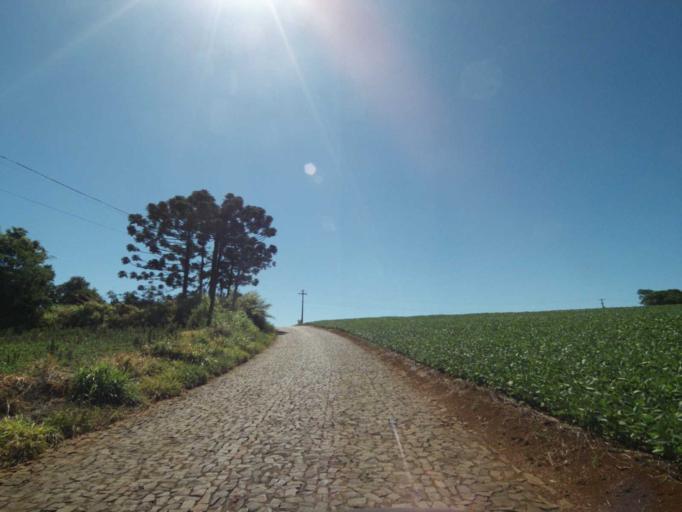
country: BR
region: Parana
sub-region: Coronel Vivida
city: Coronel Vivida
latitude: -25.9594
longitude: -52.8228
